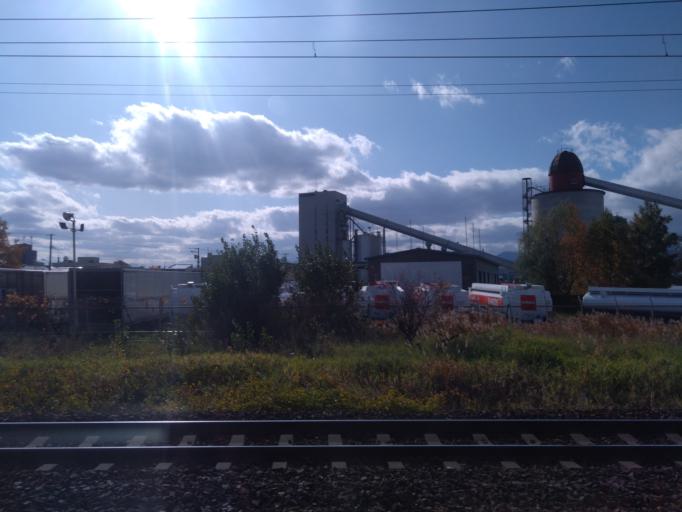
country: JP
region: Hokkaido
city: Sapporo
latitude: 43.0640
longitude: 141.3986
